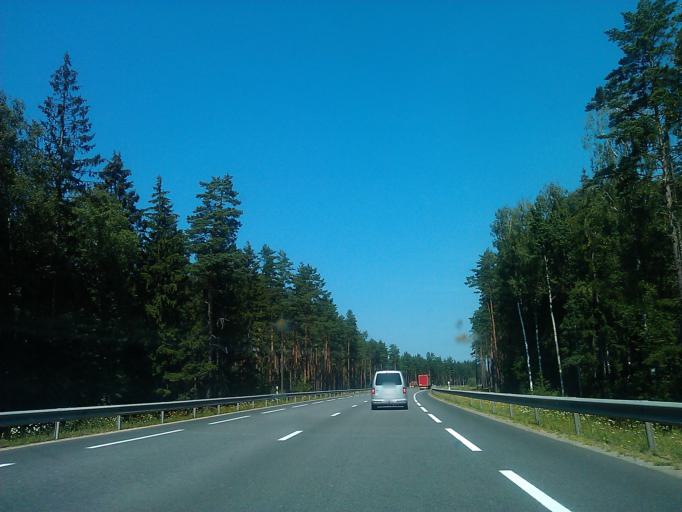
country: LV
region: Saulkrastu
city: Saulkrasti
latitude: 57.2816
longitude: 24.4335
